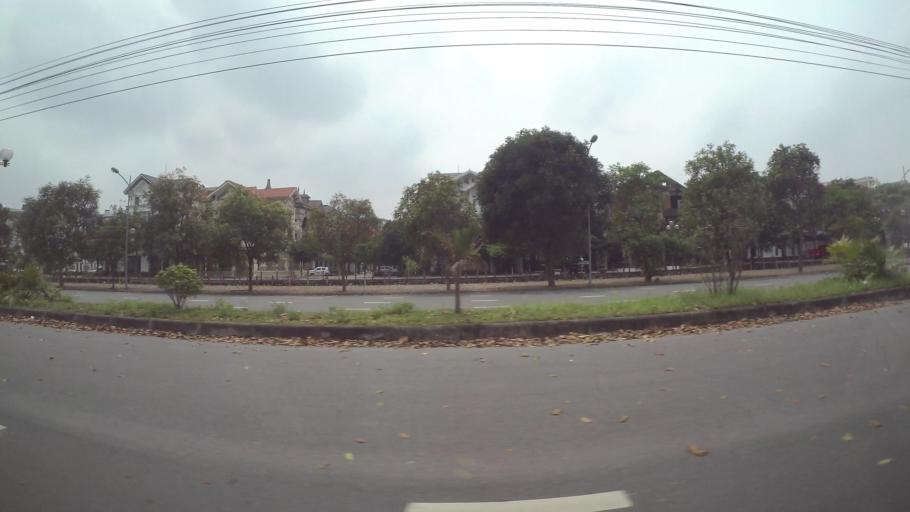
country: VN
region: Ha Noi
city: Trau Quy
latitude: 21.0673
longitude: 105.9114
